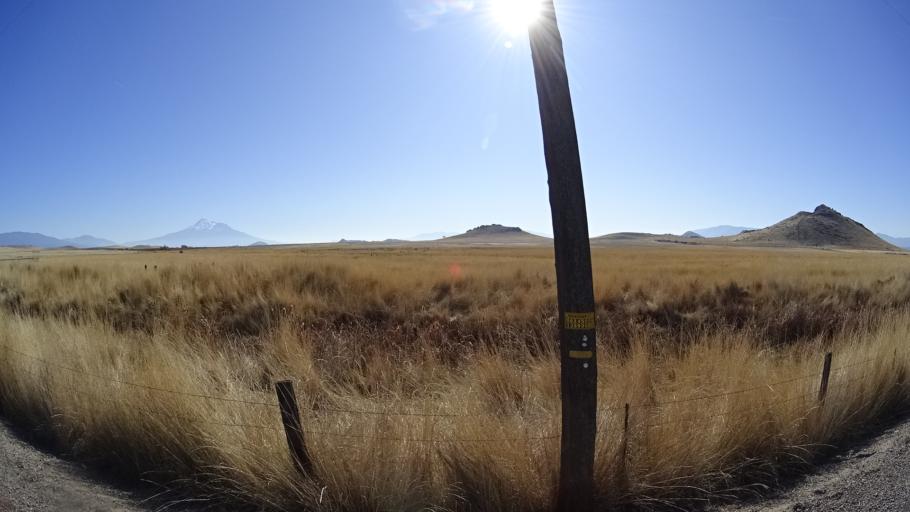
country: US
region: California
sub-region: Siskiyou County
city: Montague
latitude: 41.7562
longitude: -122.4792
